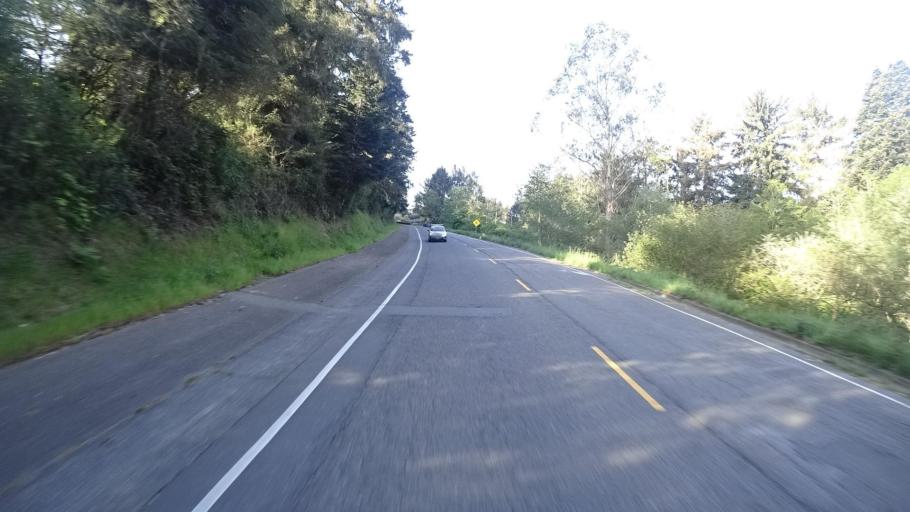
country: US
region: California
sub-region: Humboldt County
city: Humboldt Hill
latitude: 40.7283
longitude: -124.2026
